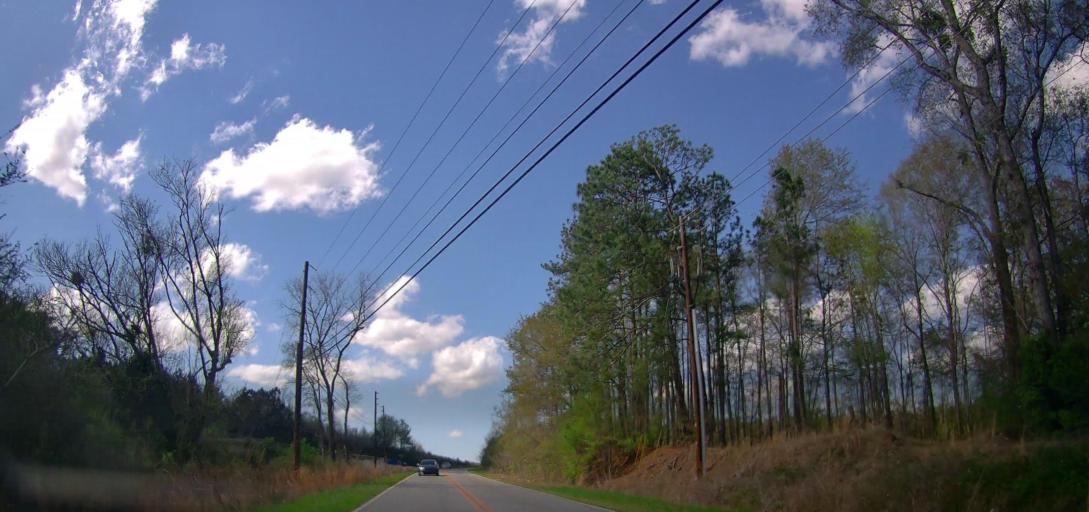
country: US
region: Georgia
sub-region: Bibb County
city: Macon
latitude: 32.8198
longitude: -83.5534
